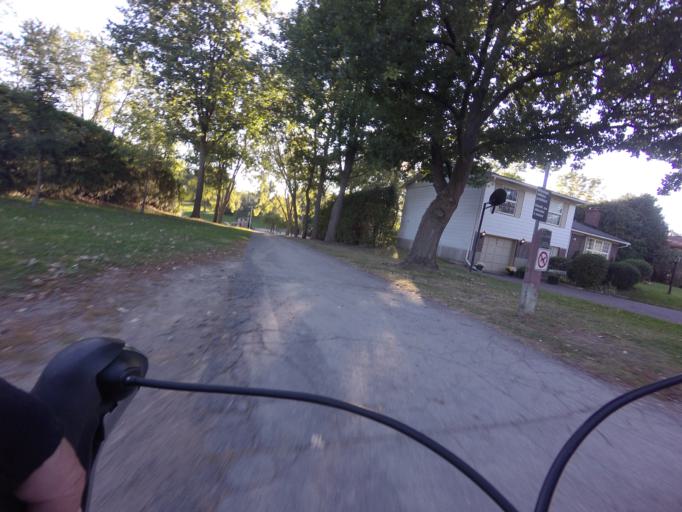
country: CA
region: Ontario
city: Bells Corners
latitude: 45.3351
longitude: -75.7878
